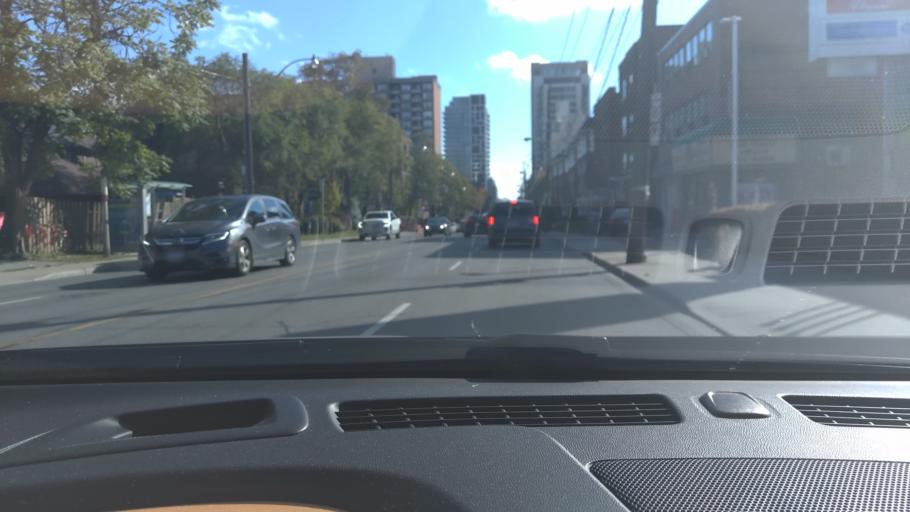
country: CA
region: Ontario
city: Toronto
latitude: 43.6870
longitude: -79.4200
